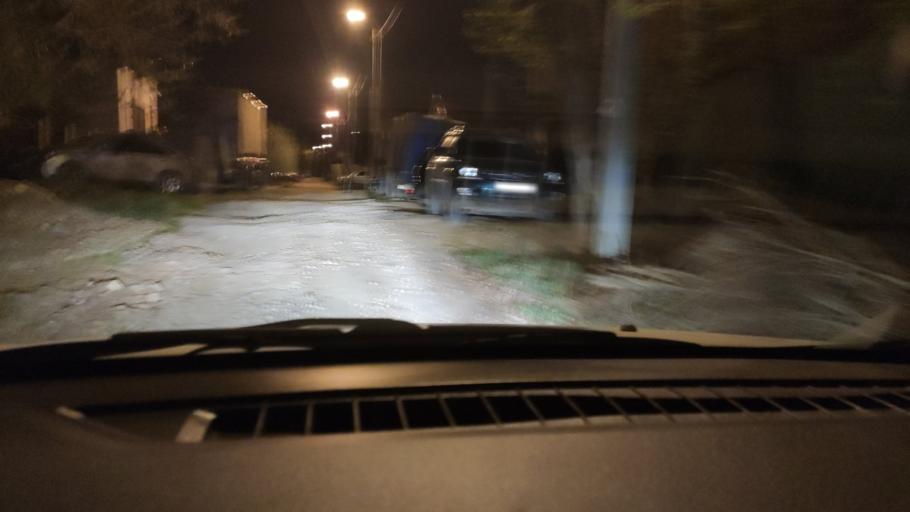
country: RU
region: Perm
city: Perm
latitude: 57.9762
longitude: 56.2913
